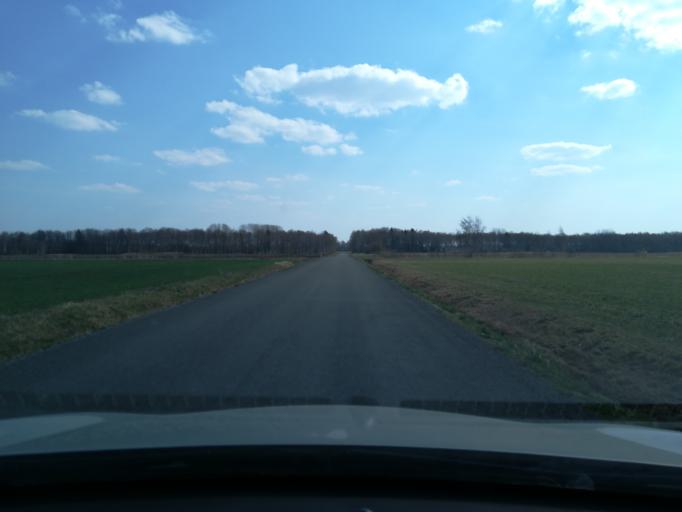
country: EE
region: Harju
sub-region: Saue linn
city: Saue
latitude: 59.3304
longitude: 24.5218
